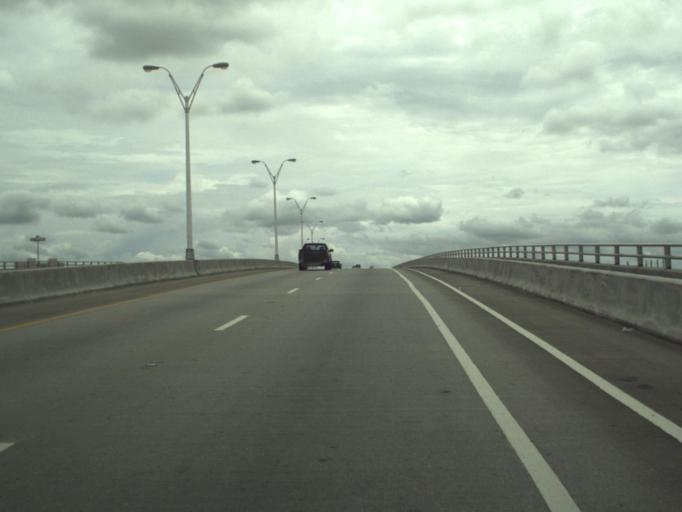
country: US
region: Florida
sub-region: Palm Beach County
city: Riviera Beach
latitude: 26.7694
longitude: -80.0554
